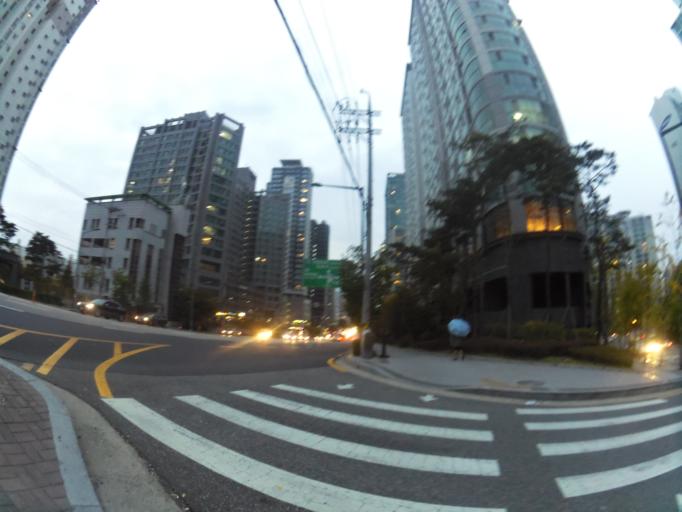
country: KR
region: Seoul
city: Seoul
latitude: 37.5423
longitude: 126.9550
